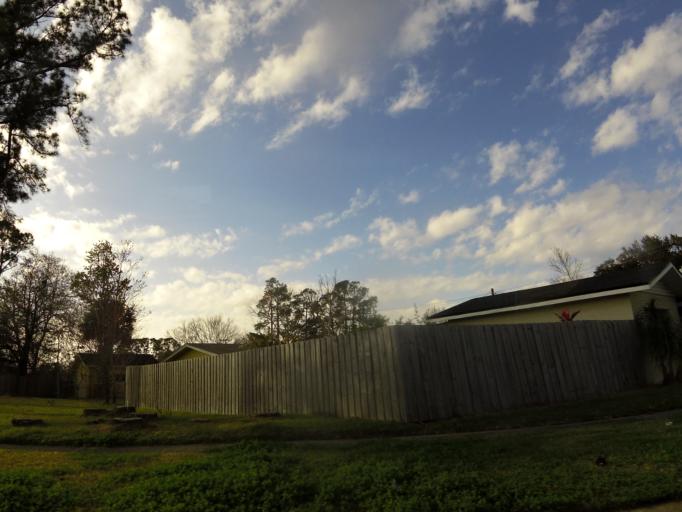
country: US
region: Florida
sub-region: Duval County
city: Jacksonville
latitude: 30.2777
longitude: -81.6052
